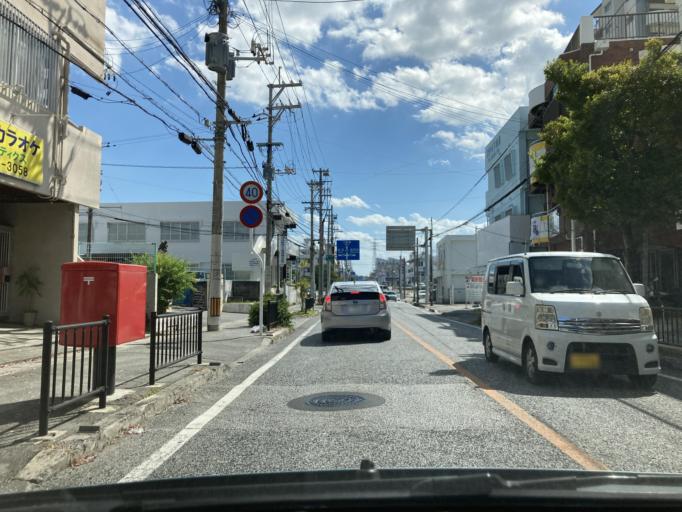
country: JP
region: Okinawa
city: Tomigusuku
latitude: 26.1936
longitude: 127.7064
